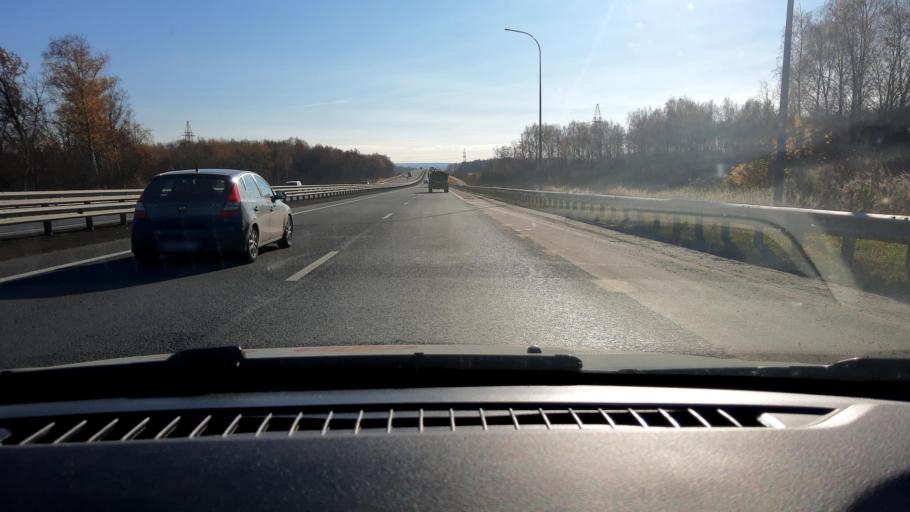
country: RU
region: Nizjnij Novgorod
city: Burevestnik
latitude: 56.1417
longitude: 43.7595
